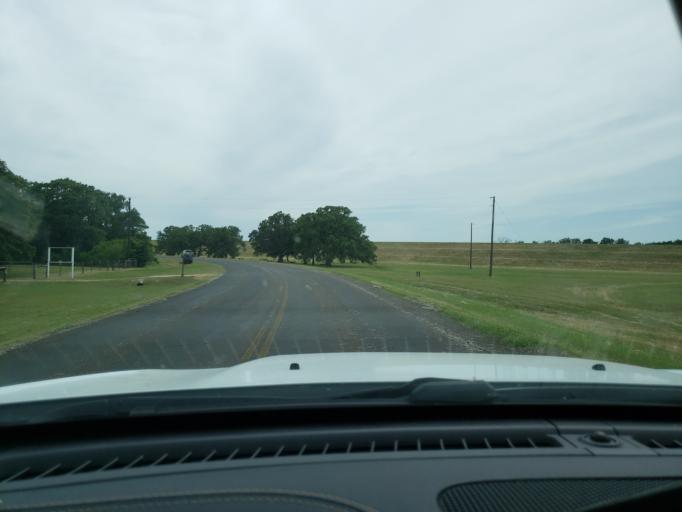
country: US
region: Texas
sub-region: Burleson County
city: Somerville
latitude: 30.3459
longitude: -96.5442
